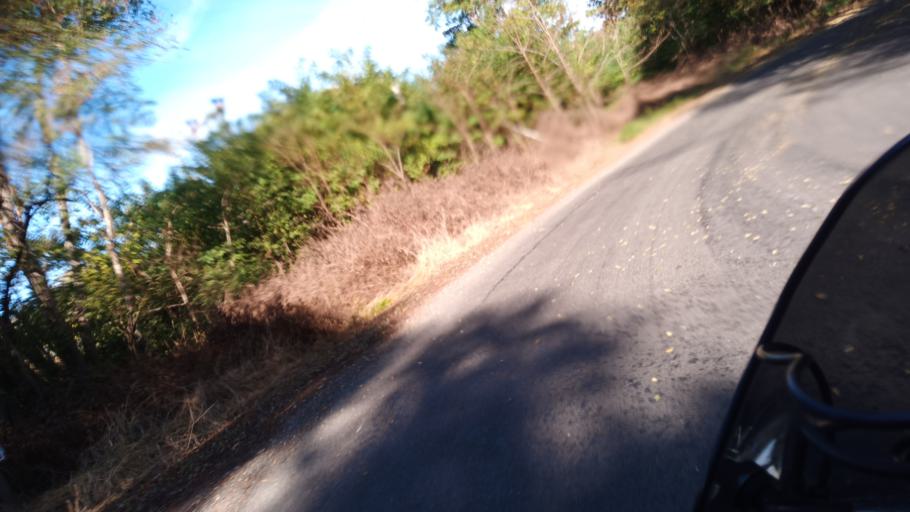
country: NZ
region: Hawke's Bay
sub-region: Wairoa District
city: Wairoa
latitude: -38.9245
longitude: 177.2629
